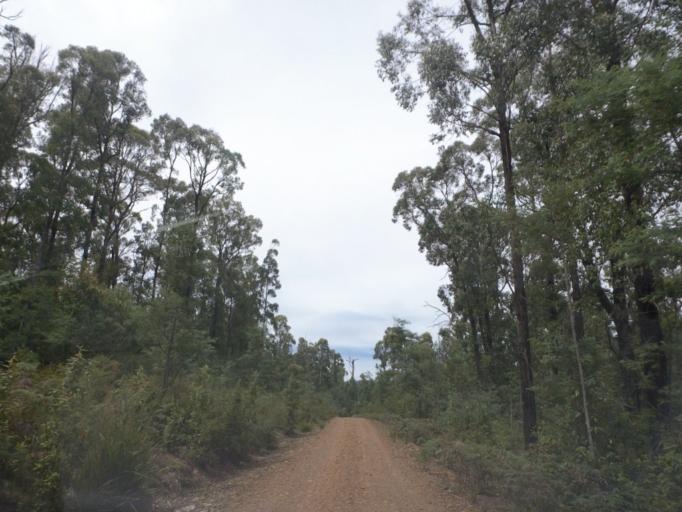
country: AU
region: Victoria
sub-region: Yarra Ranges
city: Healesville
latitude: -37.4369
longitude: 145.5807
